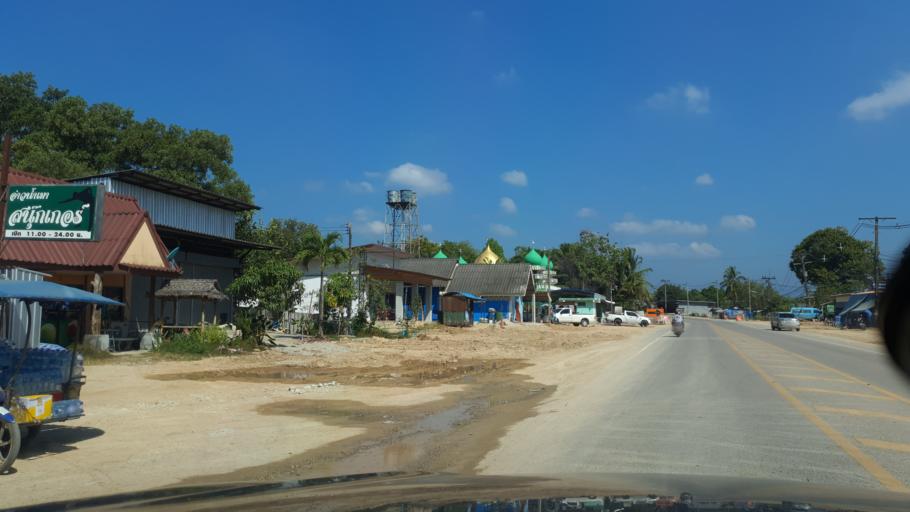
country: TH
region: Phangnga
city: Ban Ao Nang
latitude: 8.0354
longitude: 98.8616
